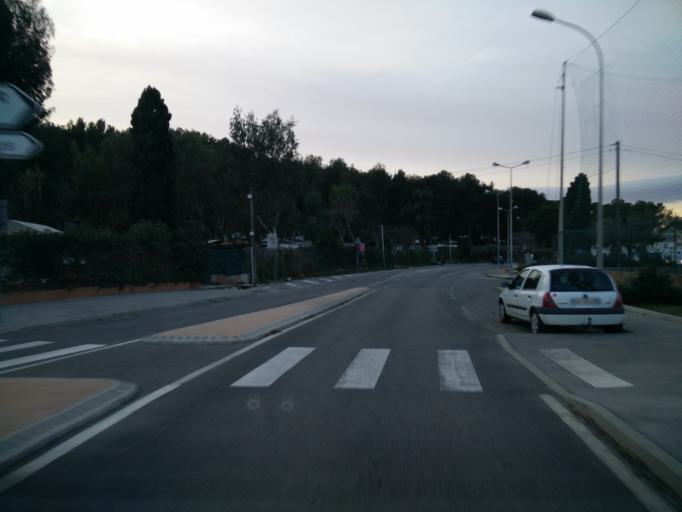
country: FR
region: Provence-Alpes-Cote d'Azur
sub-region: Departement du Var
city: Saint-Mandrier-sur-Mer
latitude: 43.0771
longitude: 5.9059
